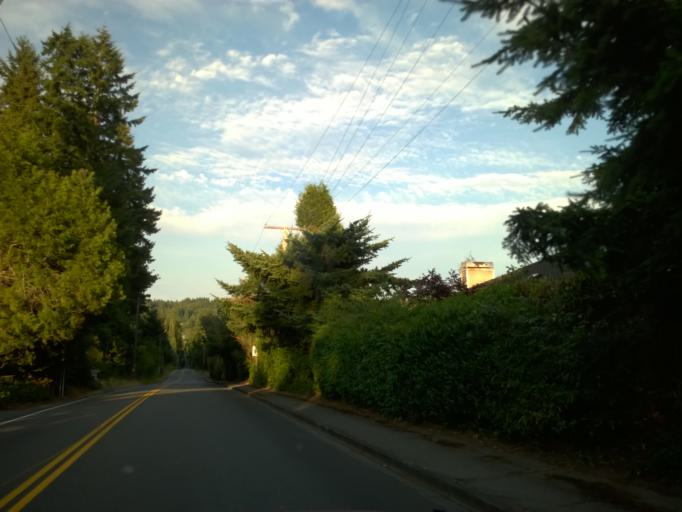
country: US
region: Washington
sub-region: King County
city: Woodinville
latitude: 47.7763
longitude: -122.1656
